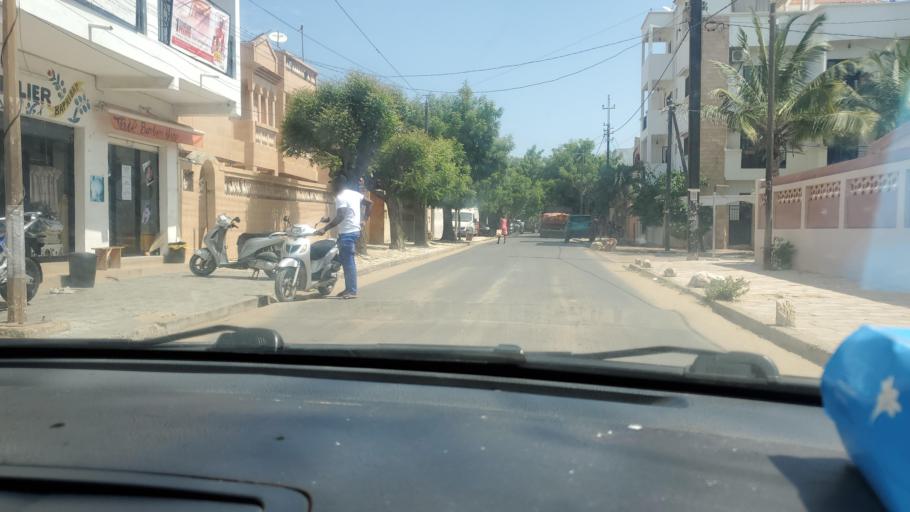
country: SN
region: Dakar
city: Grand Dakar
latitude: 14.7036
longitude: -17.4610
